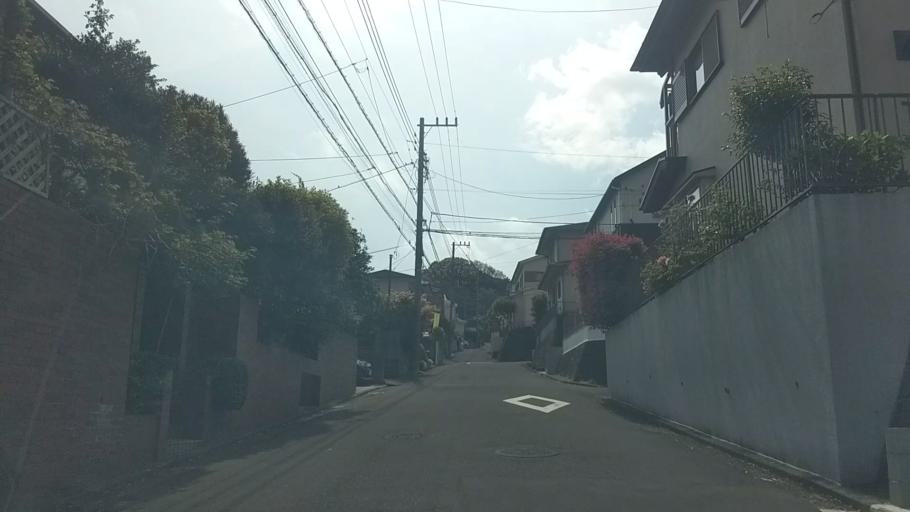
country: JP
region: Kanagawa
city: Yokohama
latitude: 35.3902
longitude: 139.5925
